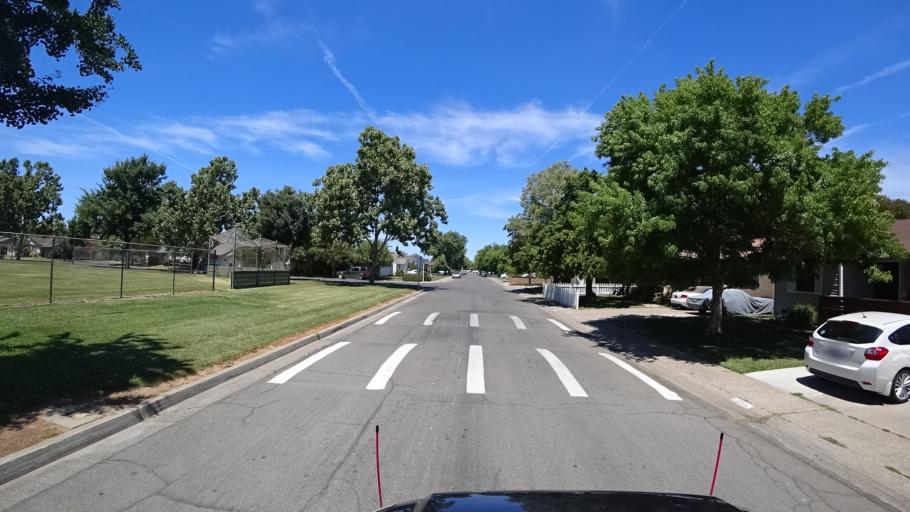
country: US
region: California
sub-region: Sacramento County
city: Parkway
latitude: 38.5217
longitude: -121.4876
